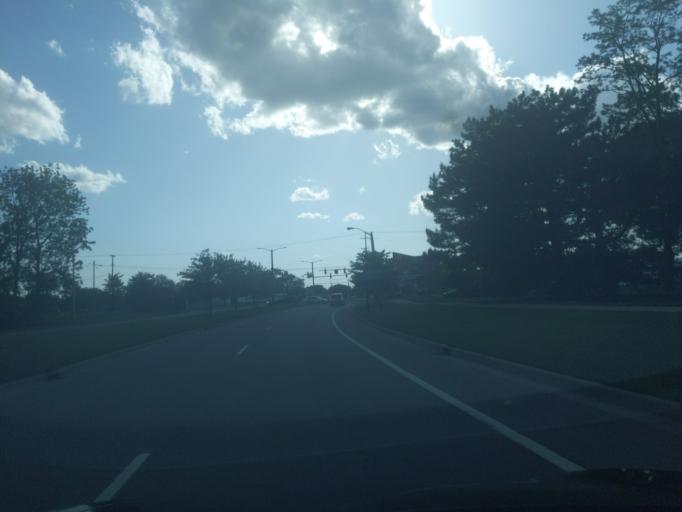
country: US
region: Michigan
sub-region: Ingham County
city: East Lansing
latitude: 42.7199
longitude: -84.4926
